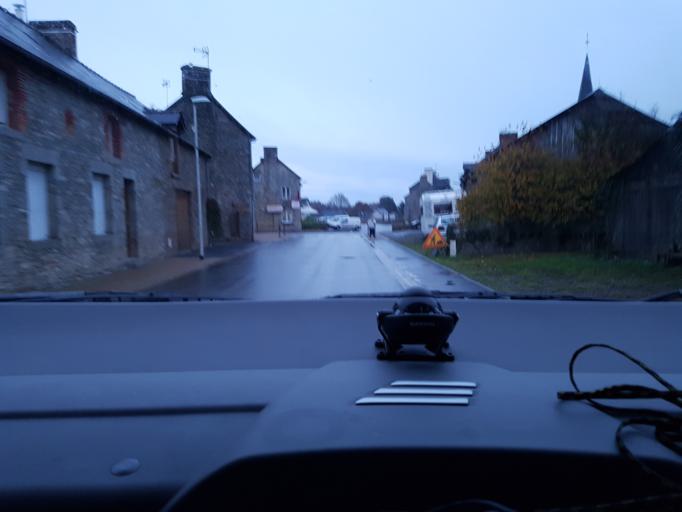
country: FR
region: Brittany
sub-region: Departement d'Ille-et-Vilaine
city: Livre-sur-Changeon
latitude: 48.2377
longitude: -1.3038
